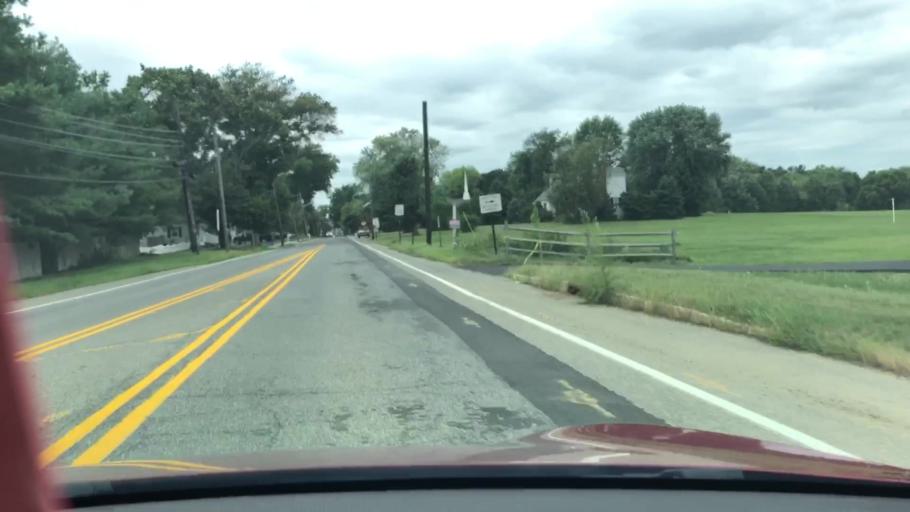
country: US
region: New Jersey
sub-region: Monmouth County
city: Allentown
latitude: 40.1767
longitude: -74.5768
